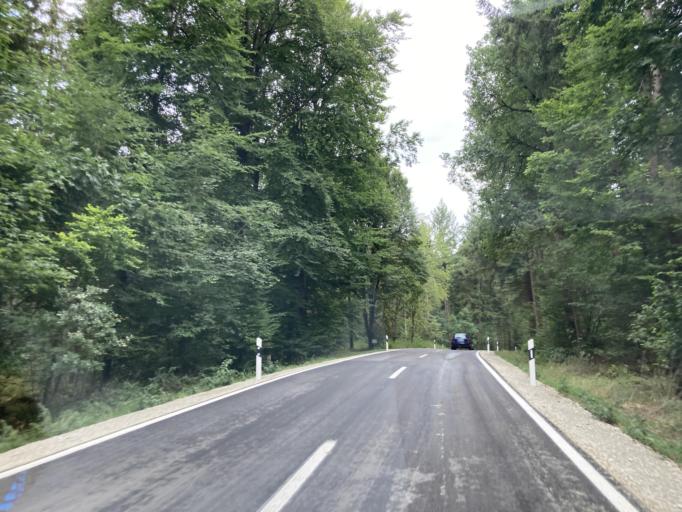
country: DE
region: Bavaria
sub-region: Swabia
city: Forheim
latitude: 48.8025
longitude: 10.4111
